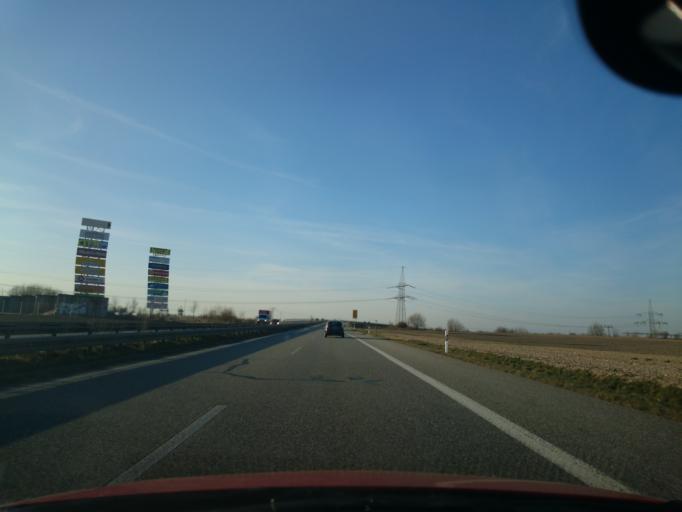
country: DE
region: Mecklenburg-Vorpommern
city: Wendorf
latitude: 54.2794
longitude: 13.0769
